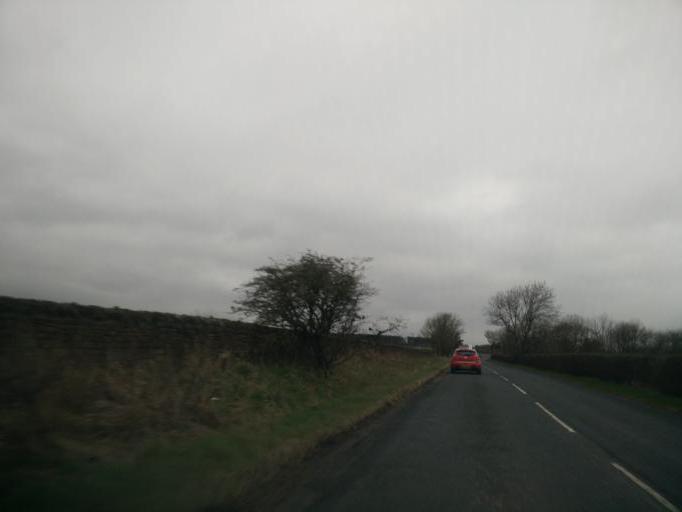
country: GB
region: England
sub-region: County Durham
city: Crook
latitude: 54.7303
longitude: -1.7091
